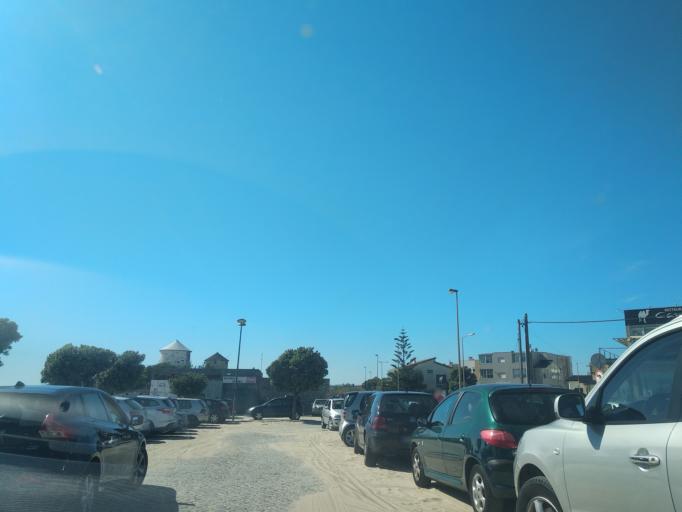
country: PT
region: Braga
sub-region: Esposende
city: Apulia
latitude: 41.4869
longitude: -8.7806
